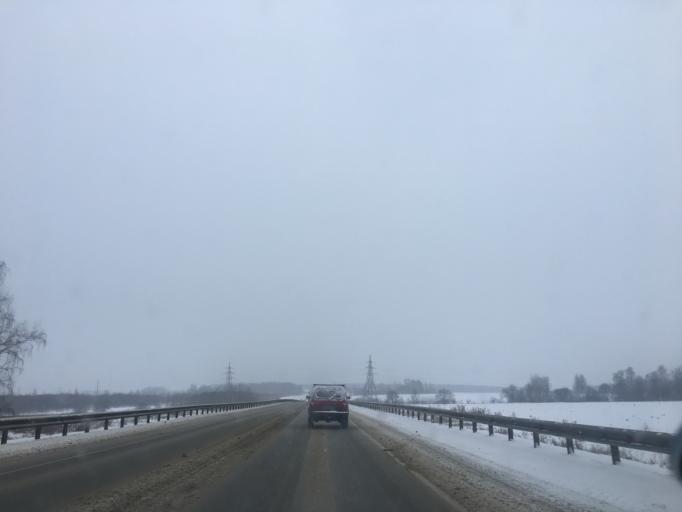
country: RU
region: Tula
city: Kosaya Gora
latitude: 54.1685
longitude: 37.4951
